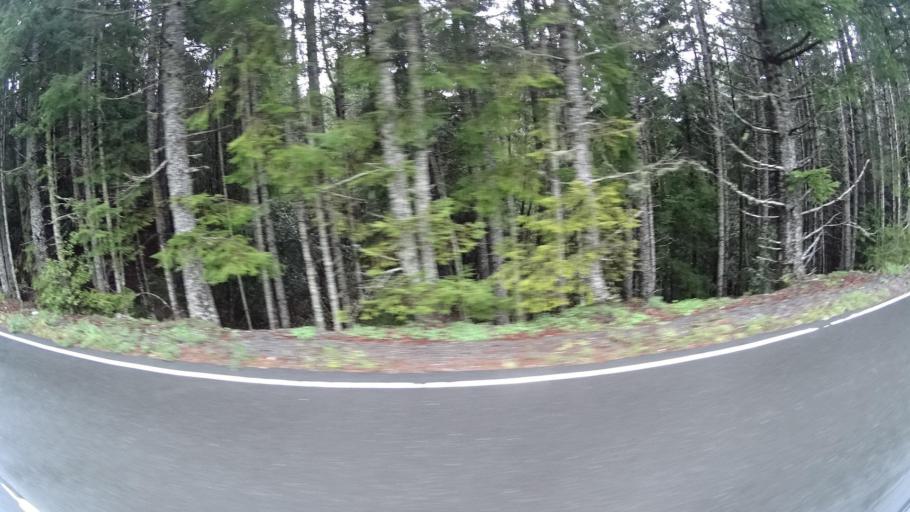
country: US
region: California
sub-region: Humboldt County
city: Westhaven-Moonstone
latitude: 41.1806
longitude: -123.9243
